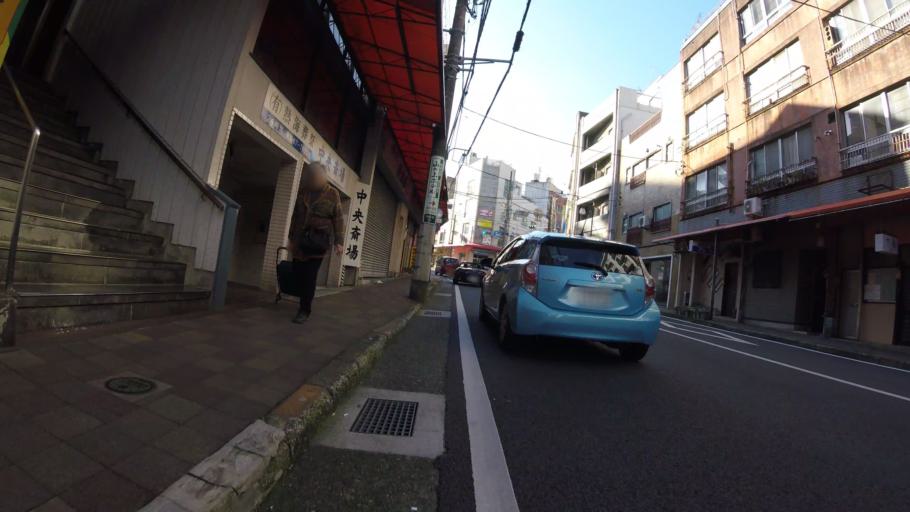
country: JP
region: Shizuoka
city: Atami
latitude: 35.0924
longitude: 139.0700
